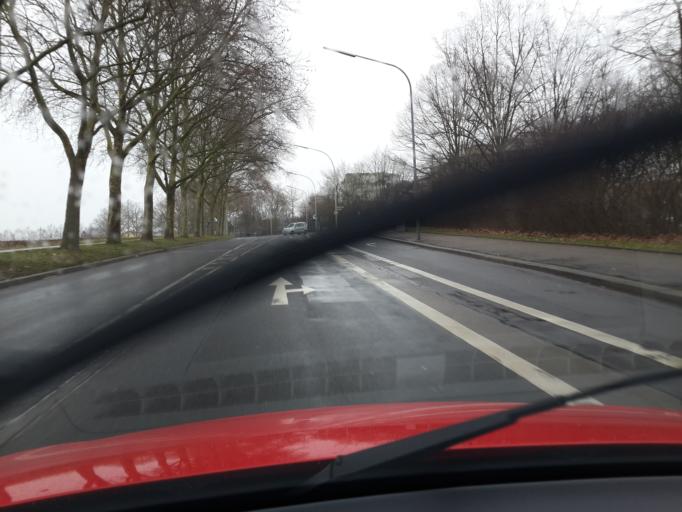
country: DE
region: Baden-Wuerttemberg
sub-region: Regierungsbezirk Stuttgart
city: Heilbronn
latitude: 49.1590
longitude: 9.1953
